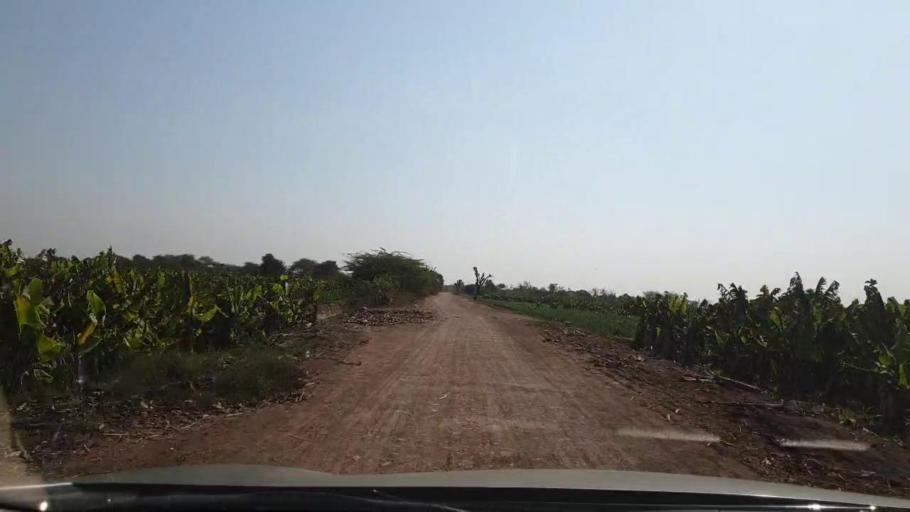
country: PK
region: Sindh
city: Mirpur Khas
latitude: 25.5965
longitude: 68.8673
